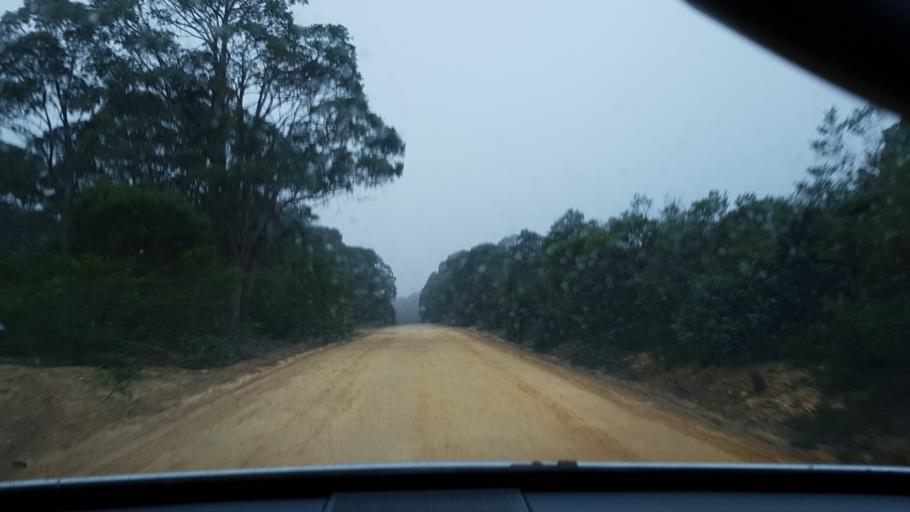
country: AU
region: New South Wales
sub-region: Blue Mountains Municipality
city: Katoomba
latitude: -33.9949
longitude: 150.0870
